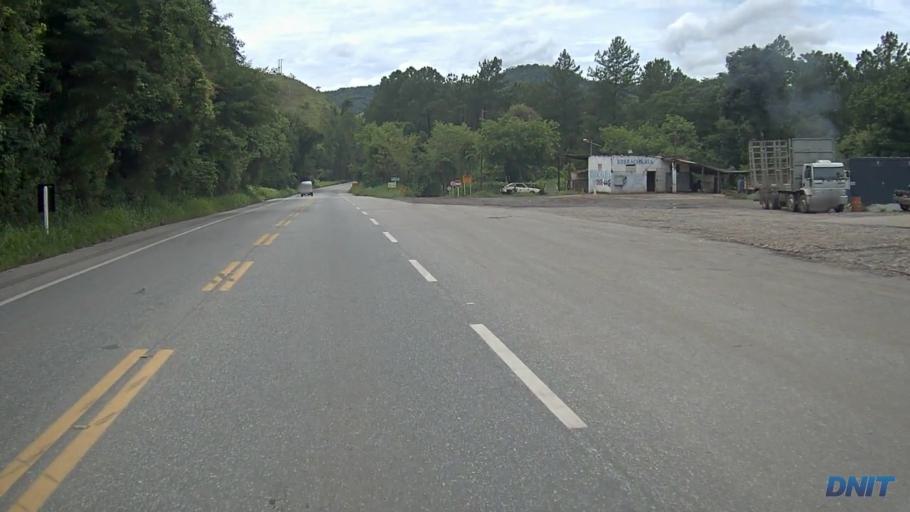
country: BR
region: Minas Gerais
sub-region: Nova Era
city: Nova Era
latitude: -19.7289
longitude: -43.0141
